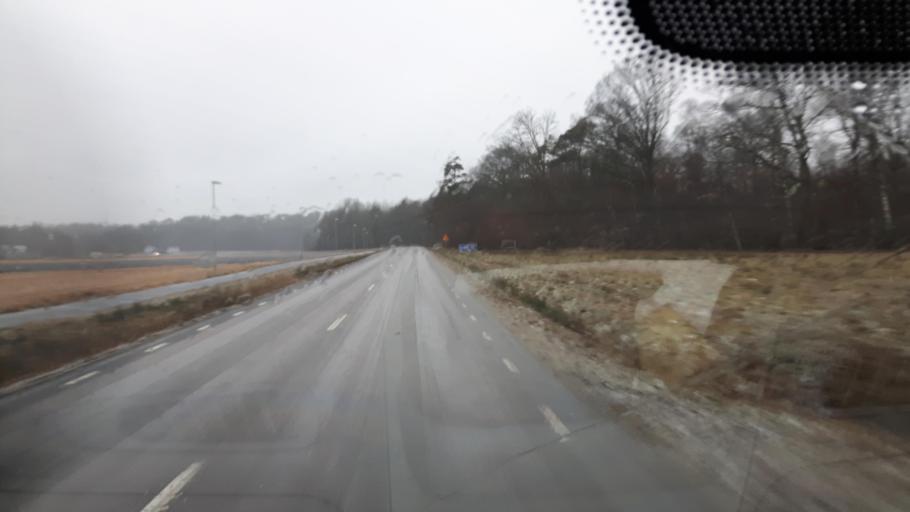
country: SE
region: Halland
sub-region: Kungsbacka Kommun
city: Vallda
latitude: 57.4605
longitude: 11.9829
